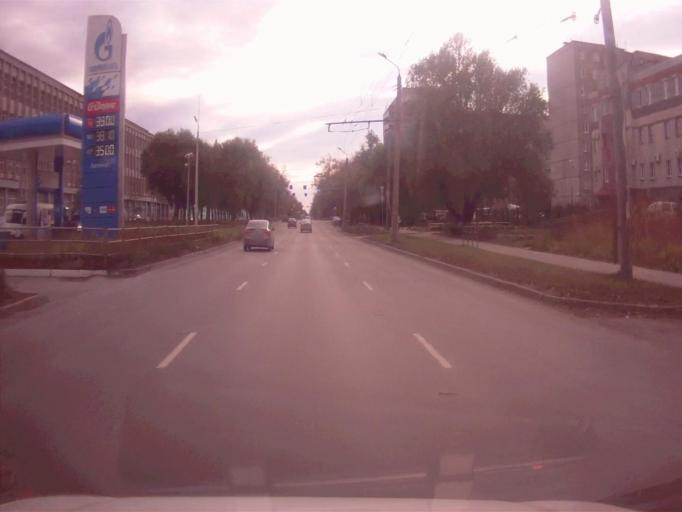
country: RU
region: Chelyabinsk
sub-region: Gorod Chelyabinsk
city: Chelyabinsk
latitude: 55.1244
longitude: 61.4747
